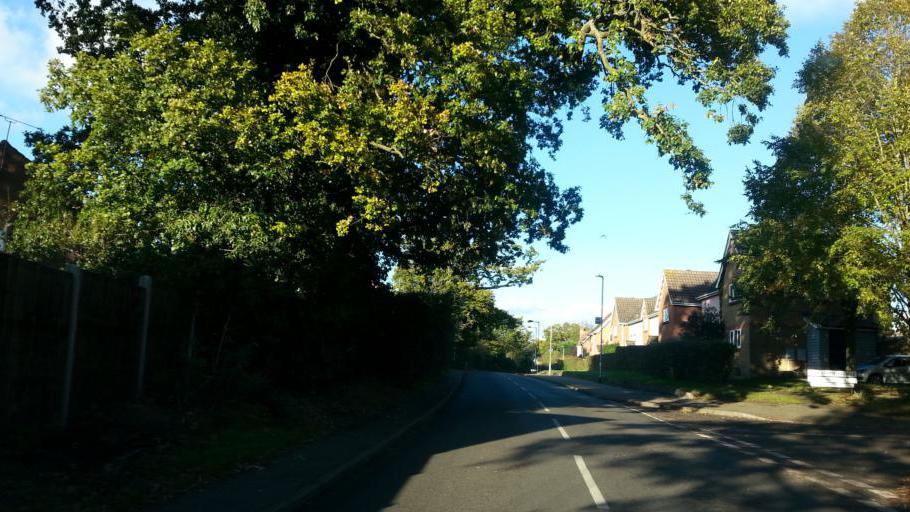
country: GB
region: England
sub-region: Suffolk
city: Thurston
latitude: 52.2513
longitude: 0.8105
